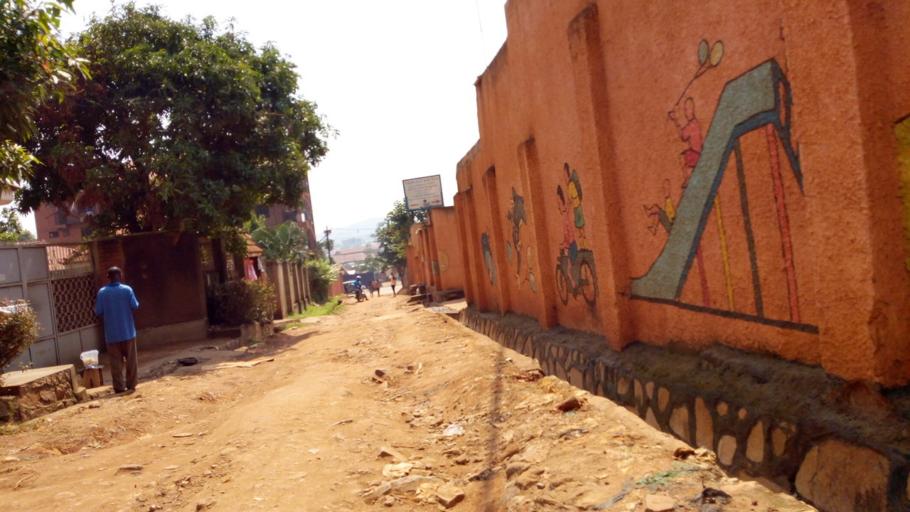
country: UG
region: Central Region
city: Kampala Central Division
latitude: 0.3459
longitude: 32.5668
